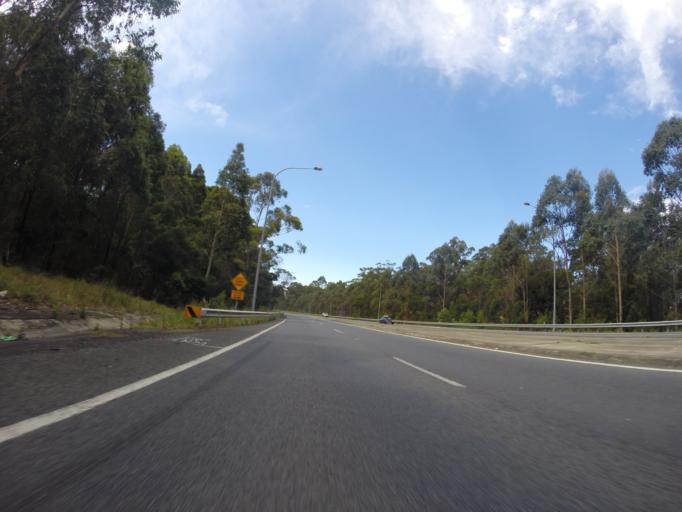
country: AU
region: New South Wales
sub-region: Shoalhaven Shire
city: Falls Creek
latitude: -35.0717
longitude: 150.5700
